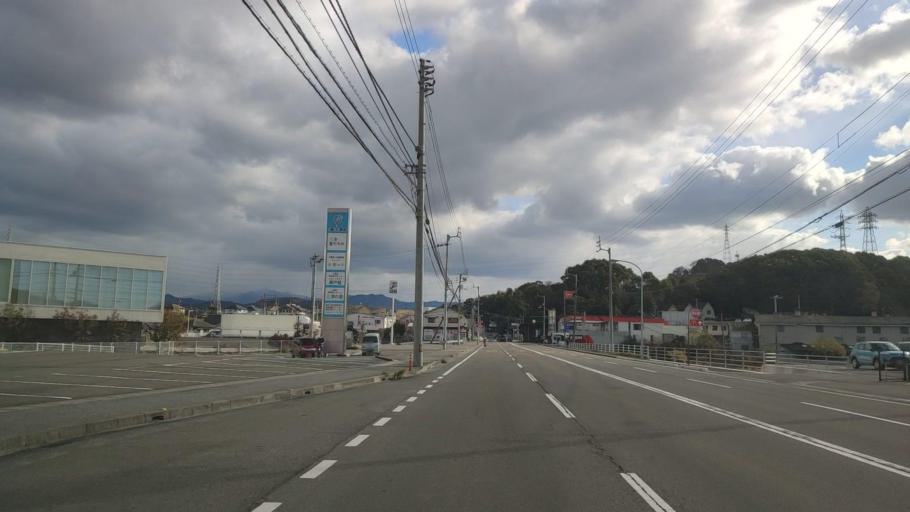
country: JP
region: Ehime
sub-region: Shikoku-chuo Shi
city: Matsuyama
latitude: 33.8565
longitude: 132.7306
